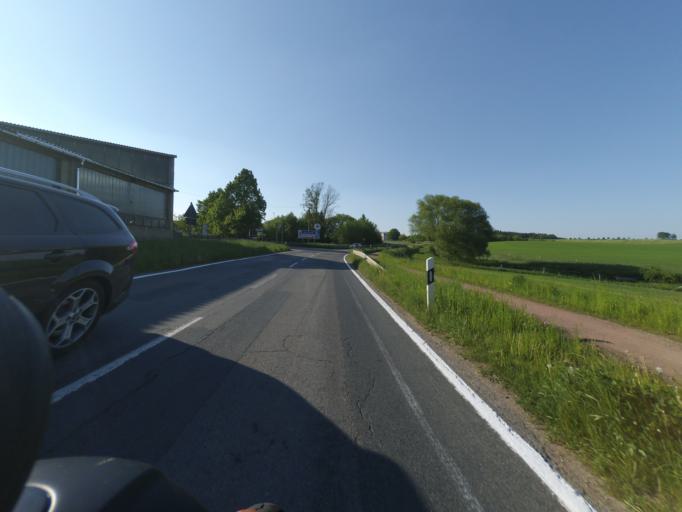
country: DE
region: Saxony
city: Dippoldiswalde
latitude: 50.8868
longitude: 13.6331
